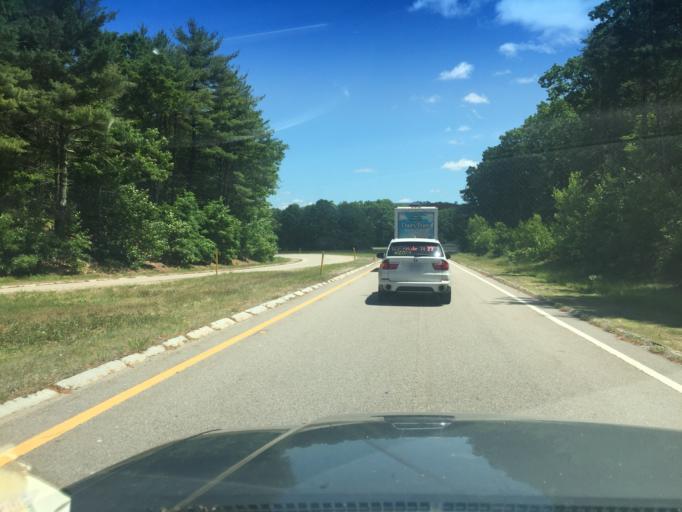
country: US
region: Massachusetts
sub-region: Bristol County
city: Mansfield
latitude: 42.0405
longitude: -71.2428
